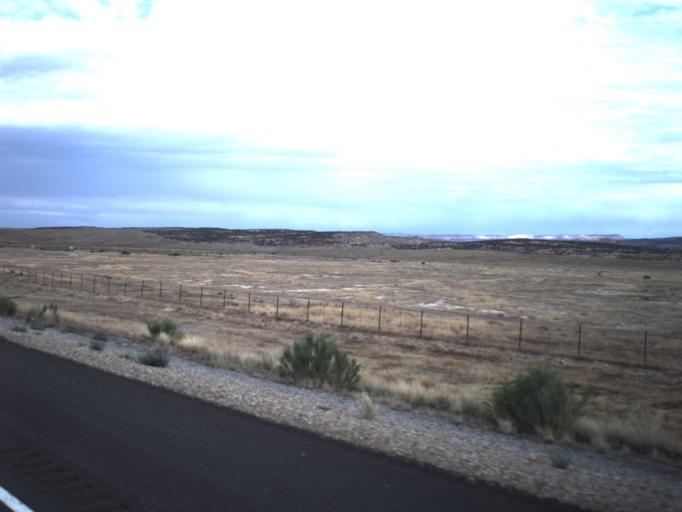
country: US
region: Colorado
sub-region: Mesa County
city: Loma
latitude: 39.0687
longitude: -109.2415
